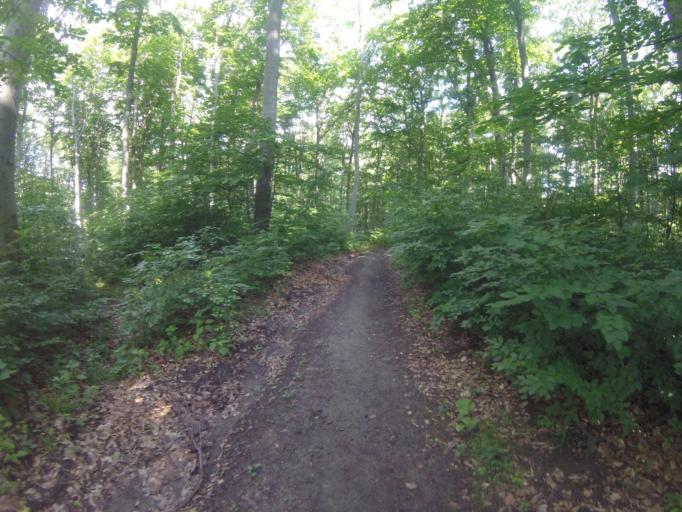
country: HU
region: Veszprem
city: Cseteny
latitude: 47.2765
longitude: 18.0343
